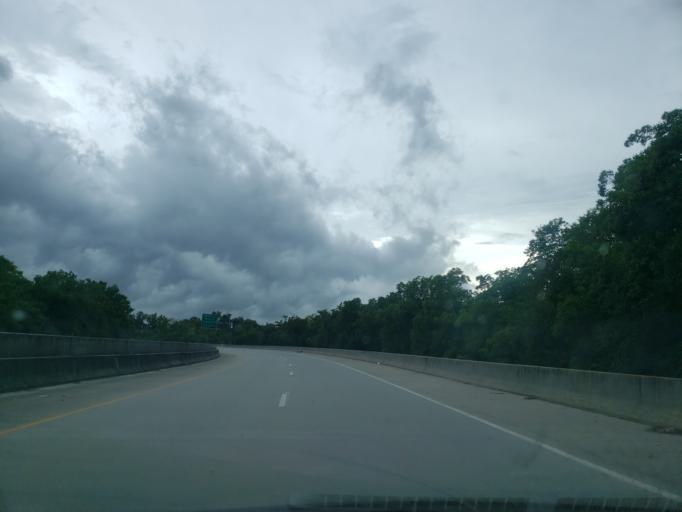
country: US
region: Georgia
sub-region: Chatham County
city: Savannah
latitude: 32.0691
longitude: -81.0758
